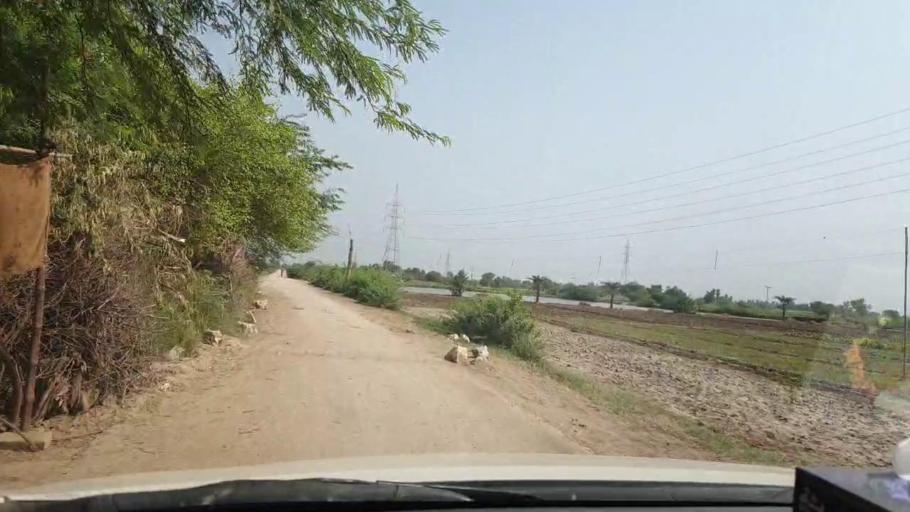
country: PK
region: Sindh
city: Shikarpur
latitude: 27.9738
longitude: 68.6650
